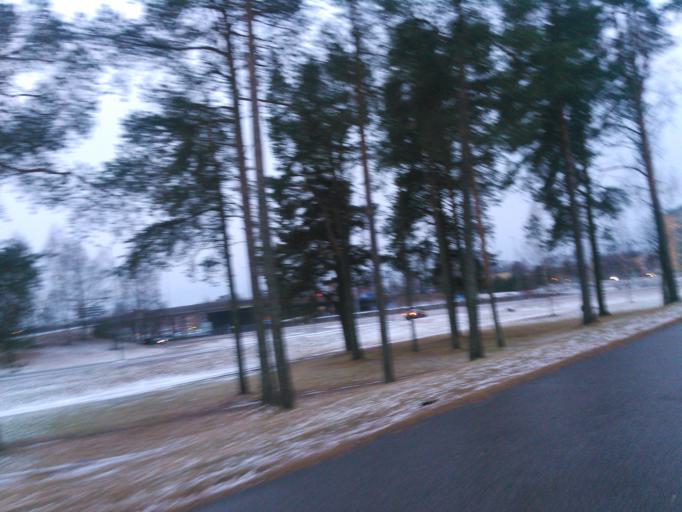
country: SE
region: Vaesterbotten
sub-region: Umea Kommun
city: Umea
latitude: 63.8334
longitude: 20.2617
